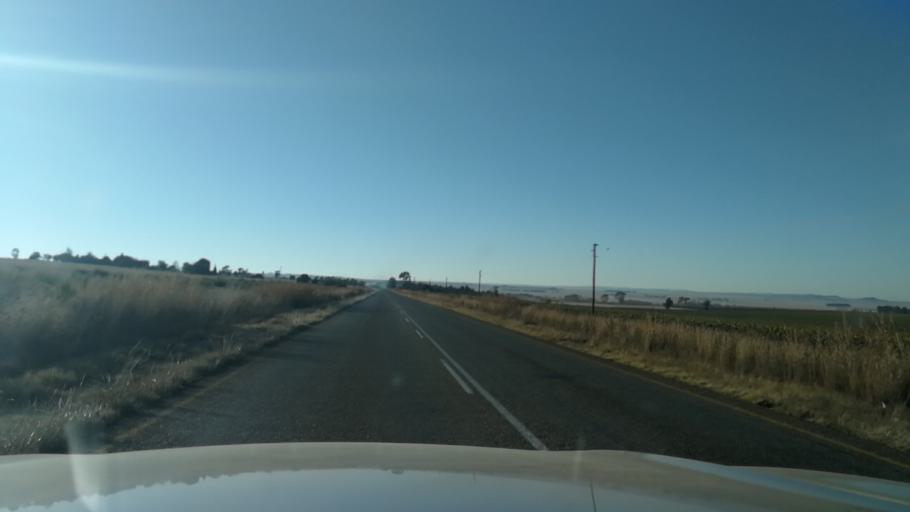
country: ZA
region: North-West
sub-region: Bojanala Platinum District Municipality
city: Koster
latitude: -25.9176
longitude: 27.0762
